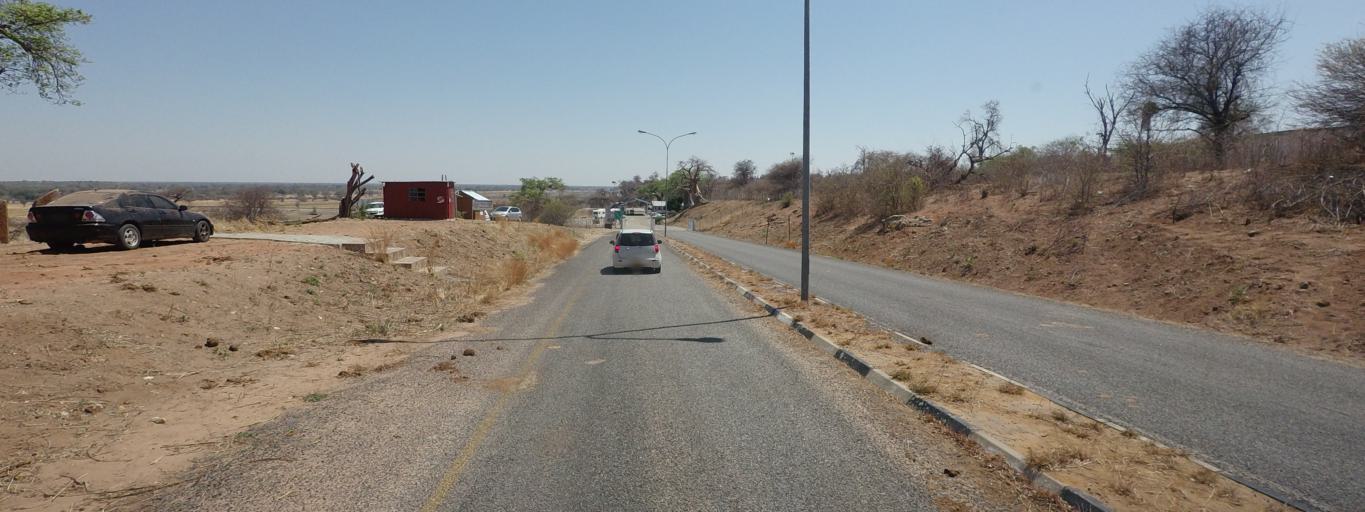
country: BW
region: North West
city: Kasane
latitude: -17.9274
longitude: 24.7200
